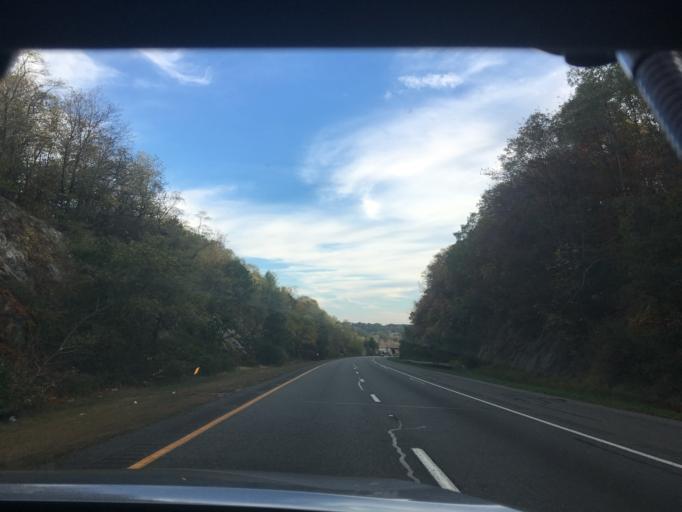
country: US
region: Rhode Island
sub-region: Providence County
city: Cranston
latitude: 41.7699
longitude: -71.4856
